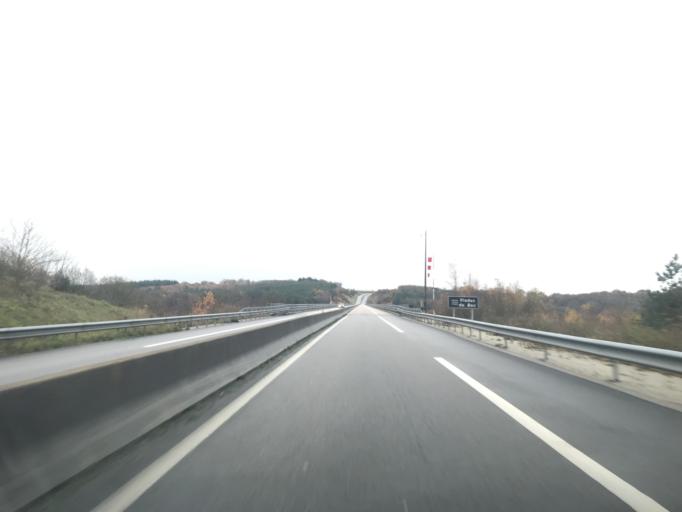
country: FR
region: Haute-Normandie
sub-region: Departement de l'Eure
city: Brionne
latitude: 49.2090
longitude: 0.7690
